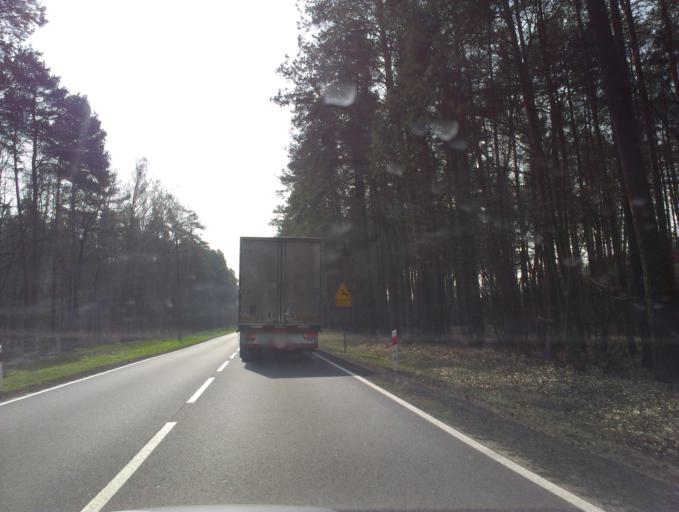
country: PL
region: Greater Poland Voivodeship
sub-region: Powiat zlotowski
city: Jastrowie
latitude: 53.3598
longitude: 16.7853
